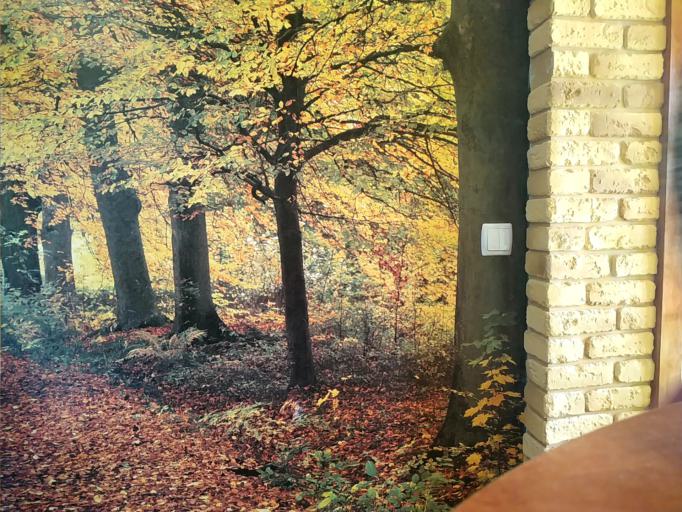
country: RU
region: Vologda
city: Molochnoye
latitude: 58.9669
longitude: 39.6350
